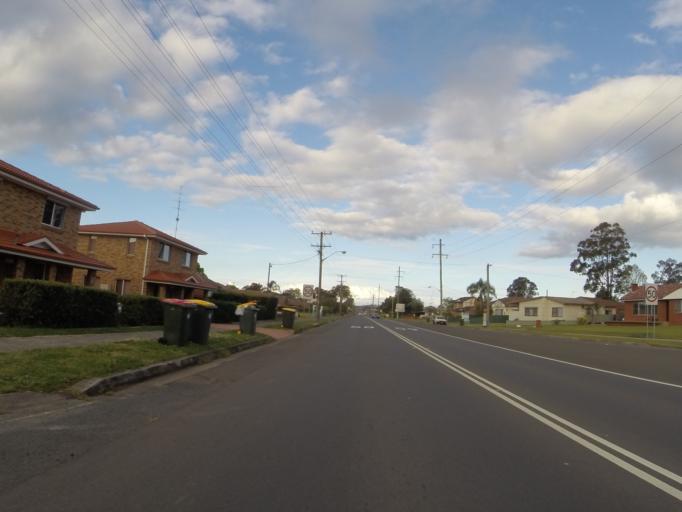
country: AU
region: New South Wales
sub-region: Shellharbour
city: Albion Park Rail
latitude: -34.5712
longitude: 150.7686
